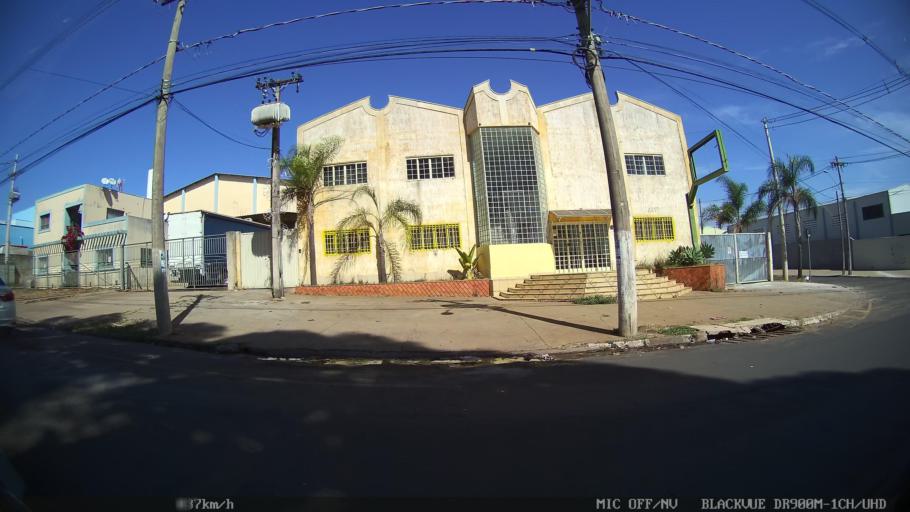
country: BR
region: Sao Paulo
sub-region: Franca
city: Franca
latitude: -20.5447
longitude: -47.4565
